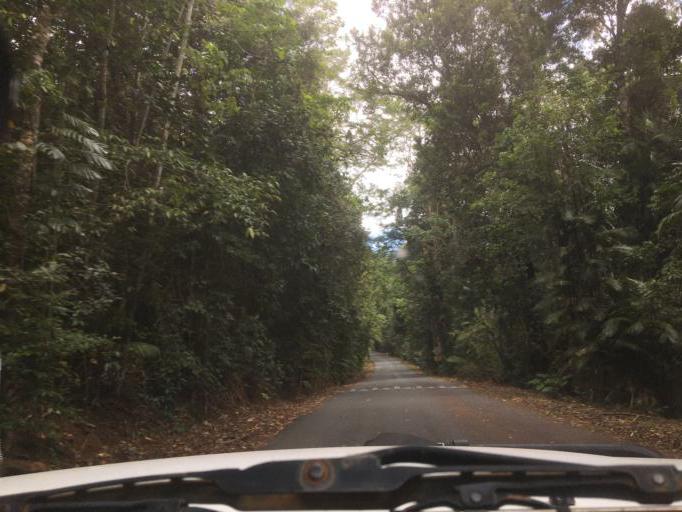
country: AU
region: Queensland
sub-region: Tablelands
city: Tolga
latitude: -17.2797
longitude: 145.6216
